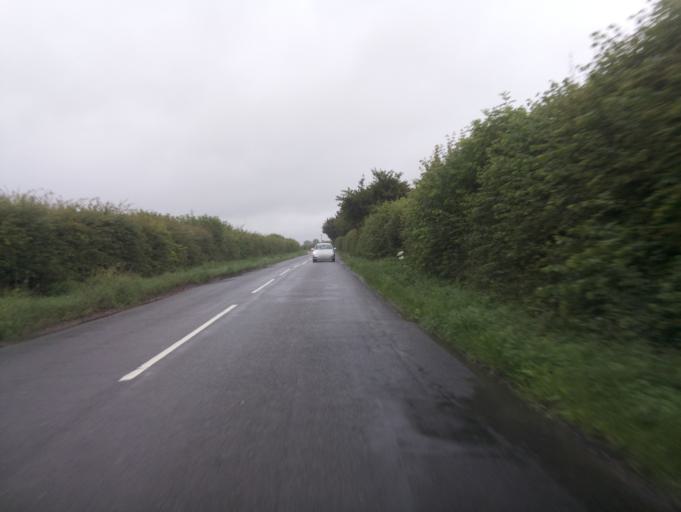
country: GB
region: England
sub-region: Gloucestershire
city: Uckington
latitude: 51.9213
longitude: -2.1394
